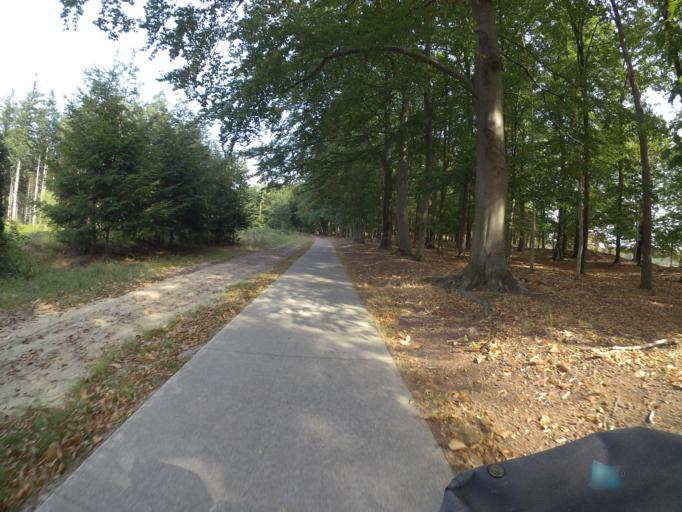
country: NL
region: Drenthe
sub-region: Gemeente Westerveld
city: Dwingeloo
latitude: 52.8878
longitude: 6.3234
